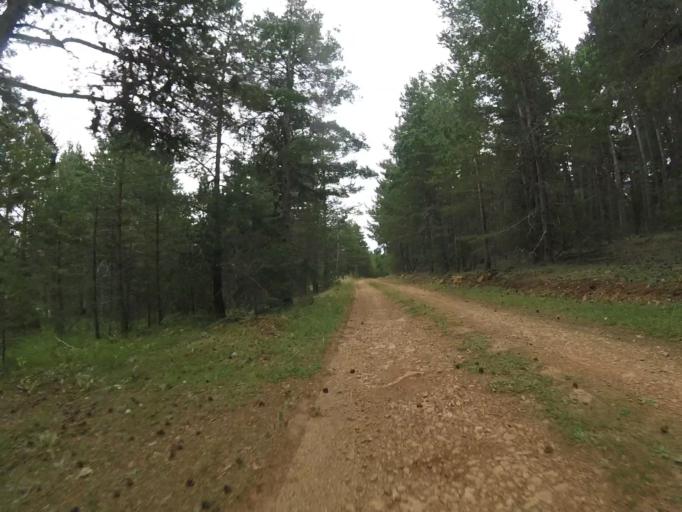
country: ES
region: Aragon
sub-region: Provincia de Teruel
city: Valdelinares
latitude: 40.3638
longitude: -0.6169
